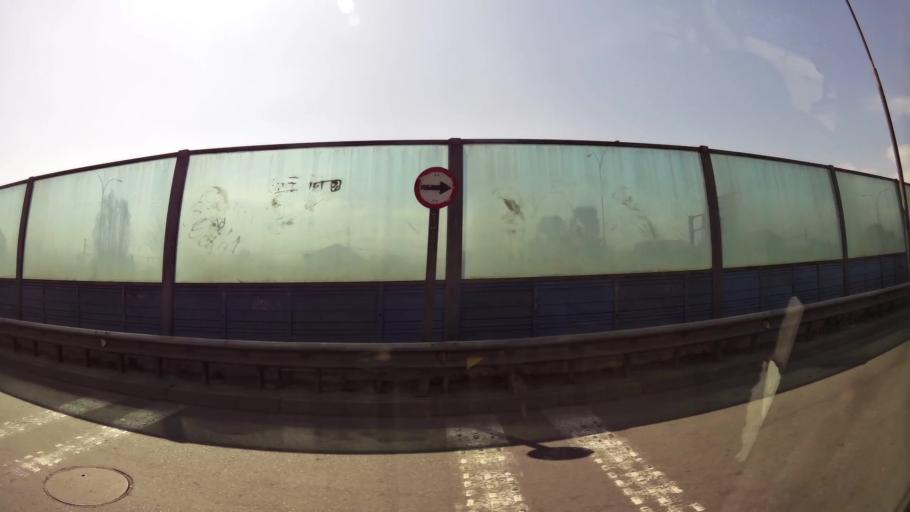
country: CL
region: Santiago Metropolitan
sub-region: Provincia de Santiago
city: Lo Prado
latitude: -33.3990
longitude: -70.6987
